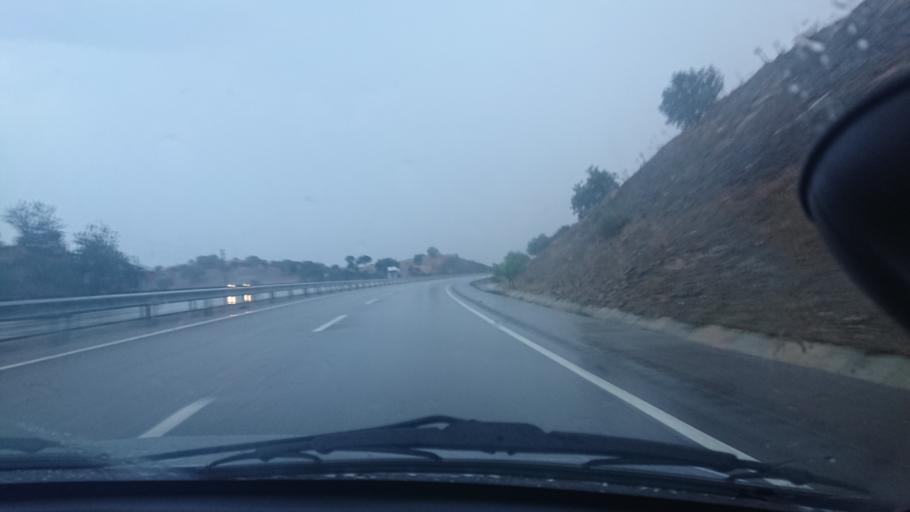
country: TR
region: Manisa
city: Menye
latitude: 38.5296
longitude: 28.4168
